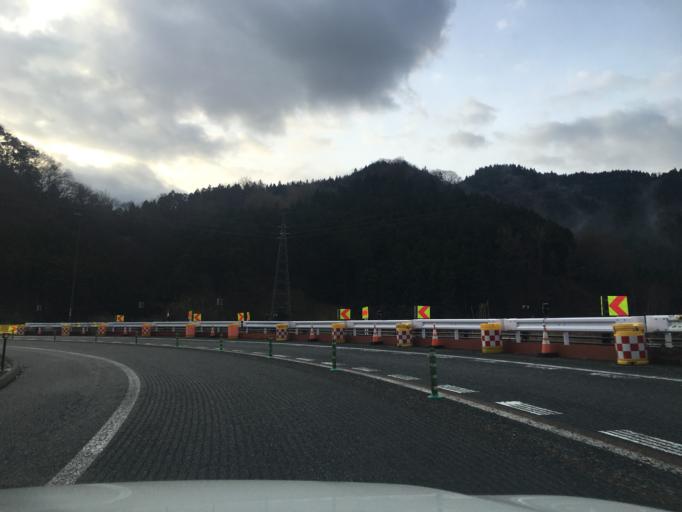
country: JP
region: Yamagata
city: Tsuruoka
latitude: 38.6030
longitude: 139.5824
